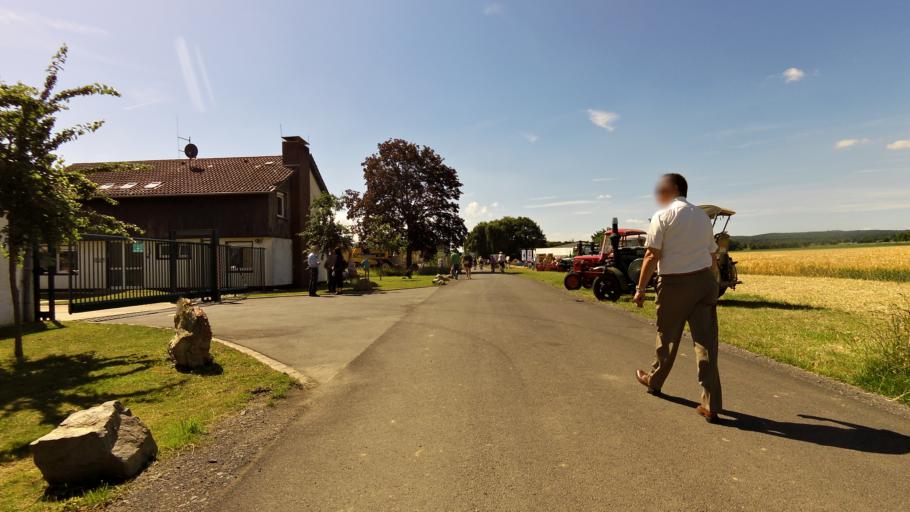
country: DE
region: North Rhine-Westphalia
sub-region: Regierungsbezirk Koln
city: Rheinbach
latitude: 50.6254
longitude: 6.9883
